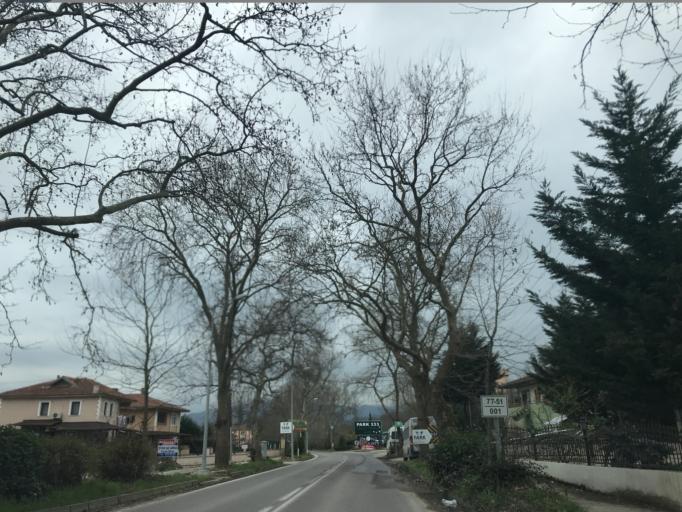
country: TR
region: Yalova
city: Kadikoy
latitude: 40.6380
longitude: 29.2263
